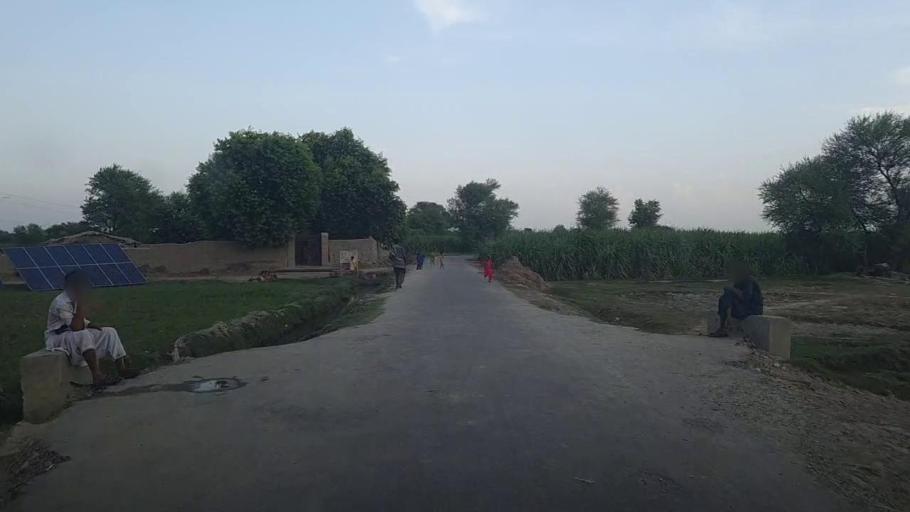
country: PK
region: Sindh
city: Ubauro
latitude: 28.3587
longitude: 69.7836
